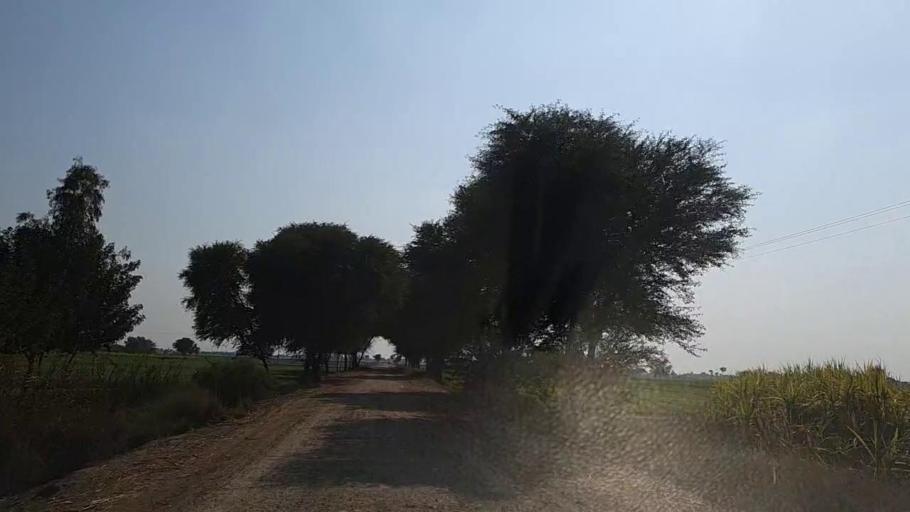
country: PK
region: Sindh
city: Daur
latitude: 26.4492
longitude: 68.2347
